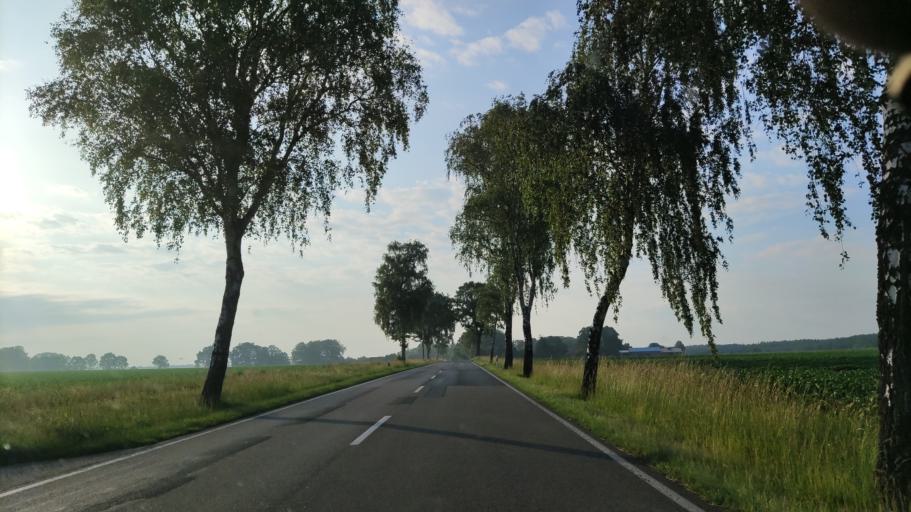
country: DE
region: Lower Saxony
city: Rehlingen
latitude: 53.0946
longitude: 10.2637
